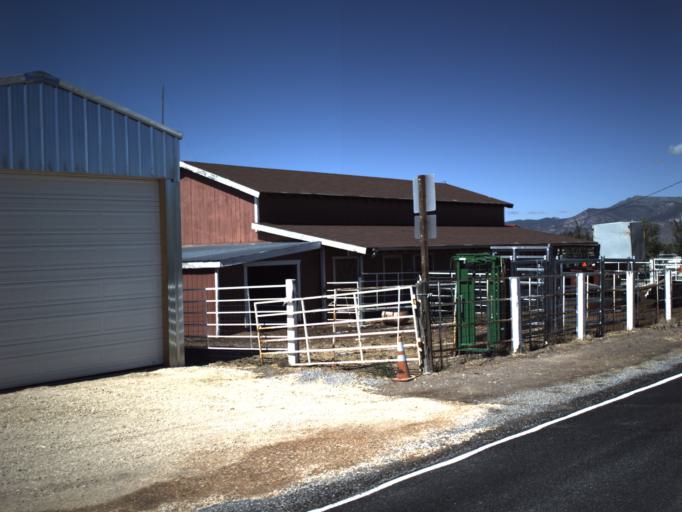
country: US
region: Utah
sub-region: Piute County
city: Junction
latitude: 38.0927
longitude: -111.9831
